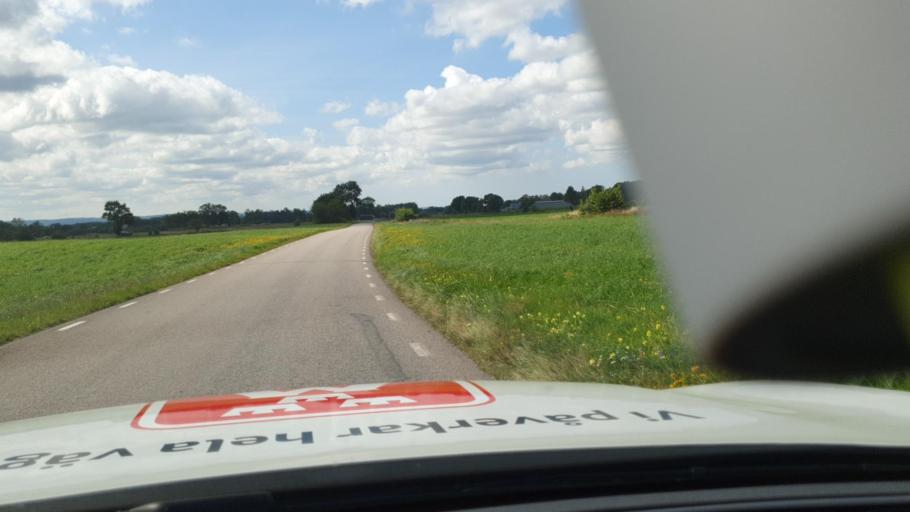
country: SE
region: Halland
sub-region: Laholms Kommun
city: Knared
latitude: 56.4615
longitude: 13.1897
